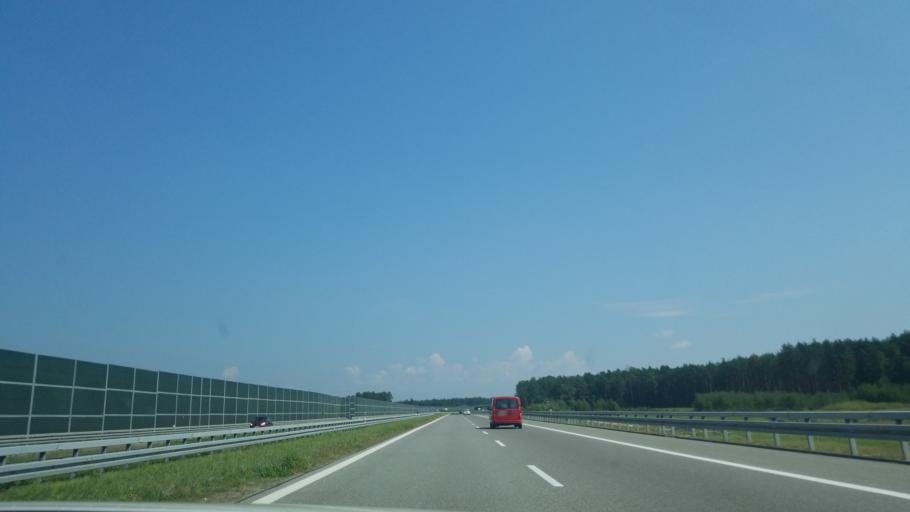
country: PL
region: Subcarpathian Voivodeship
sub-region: Powiat rzeszowski
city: Trzciana
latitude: 50.1167
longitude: 21.7814
